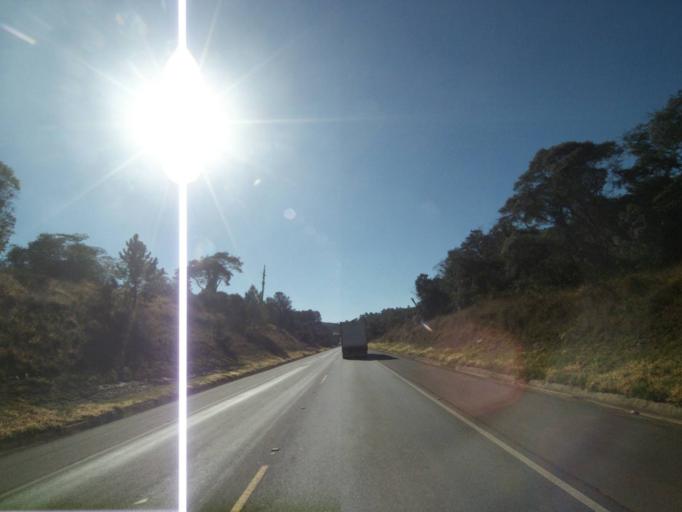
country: BR
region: Parana
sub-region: Tibagi
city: Tibagi
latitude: -24.5726
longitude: -50.4514
